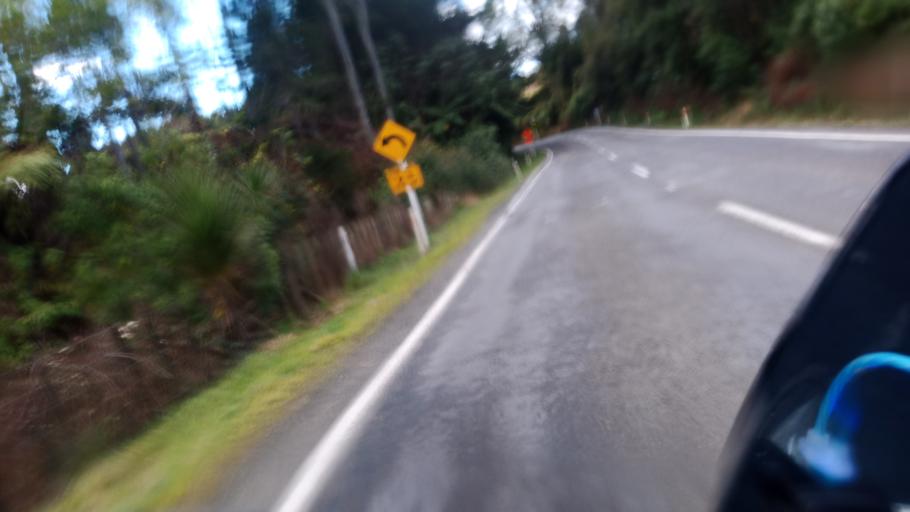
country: NZ
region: Gisborne
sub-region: Gisborne District
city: Gisborne
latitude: -38.0621
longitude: 178.3055
